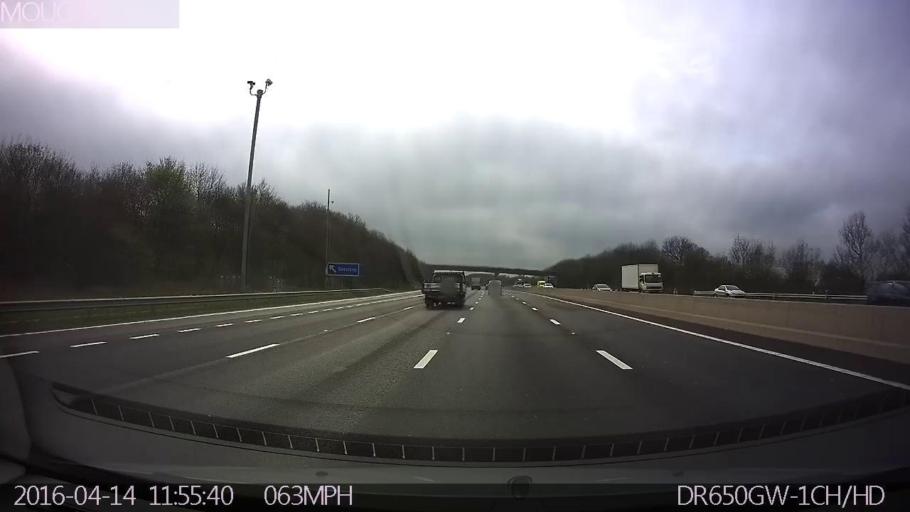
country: GB
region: England
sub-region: Derbyshire
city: Tibshelf
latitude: 53.1414
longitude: -1.3310
